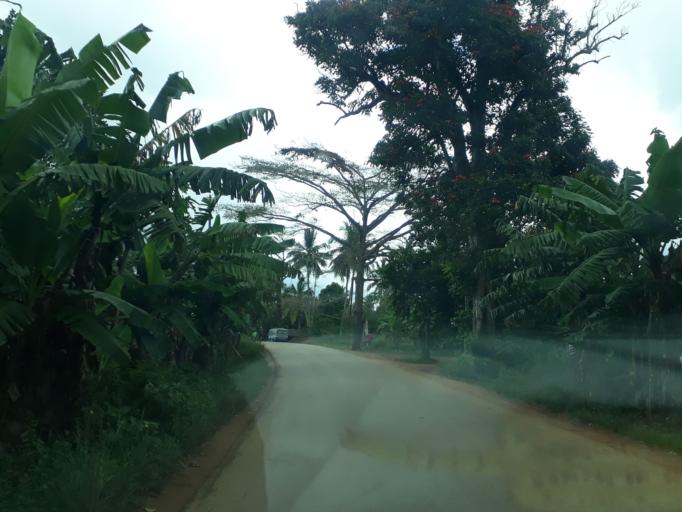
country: TZ
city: Kiwengwa
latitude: -5.9753
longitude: 39.3114
